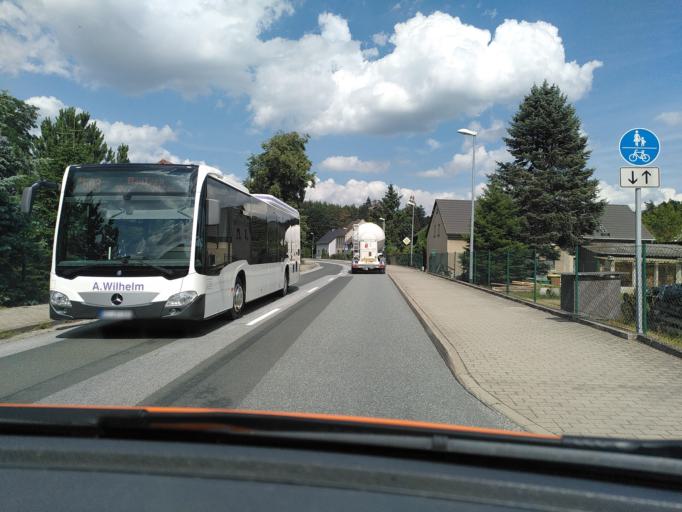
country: DE
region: Saxony
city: Malschwitz
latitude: 51.2935
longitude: 14.5098
